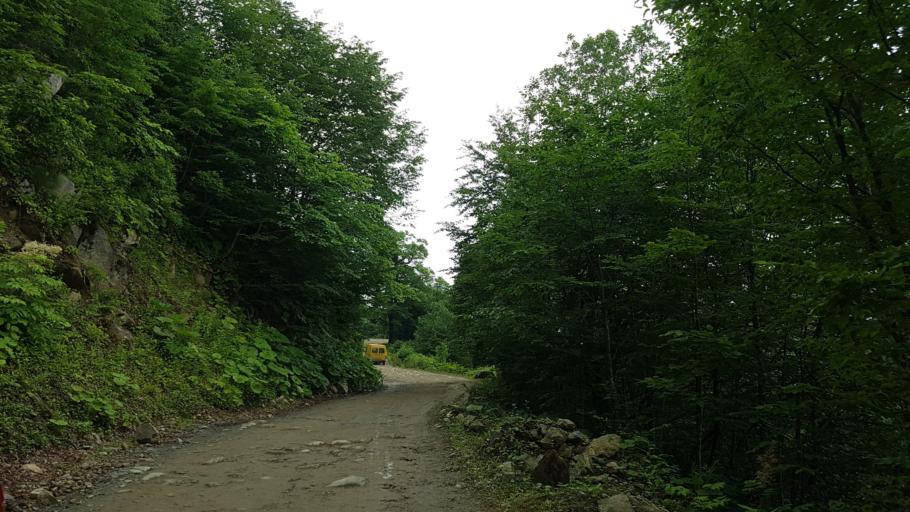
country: GE
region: Guria
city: Ozurgeti
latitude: 41.8414
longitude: 42.1321
